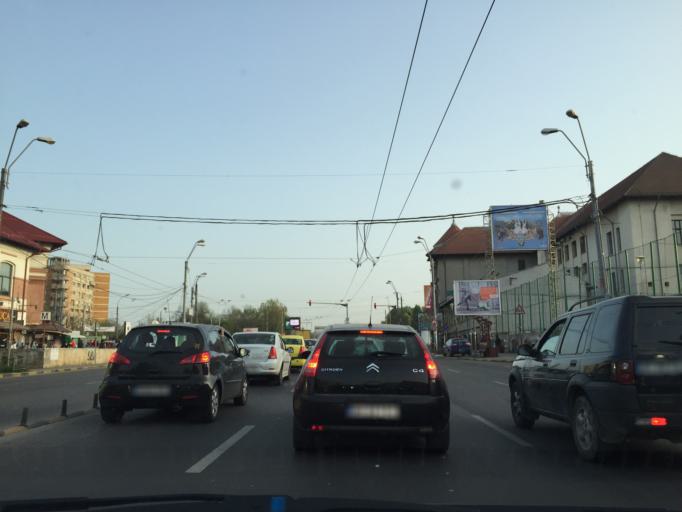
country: RO
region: Bucuresti
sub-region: Municipiul Bucuresti
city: Bucuresti
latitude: 44.4151
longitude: 26.1044
